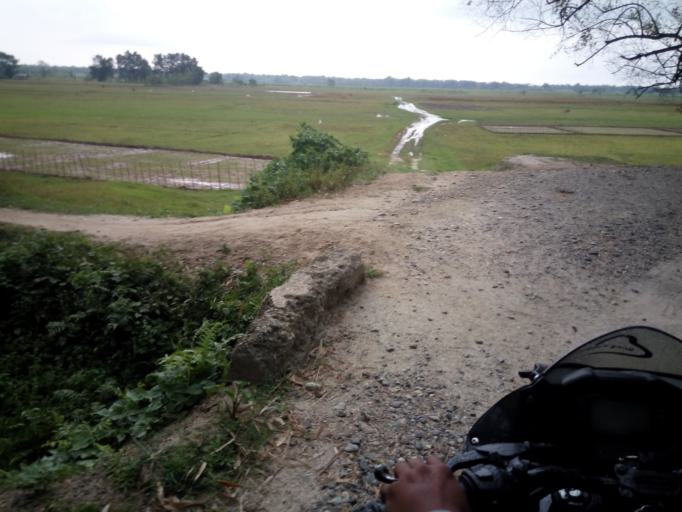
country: IN
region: Assam
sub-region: Darrang
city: Kharupatia
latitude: 26.6512
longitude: 92.2456
